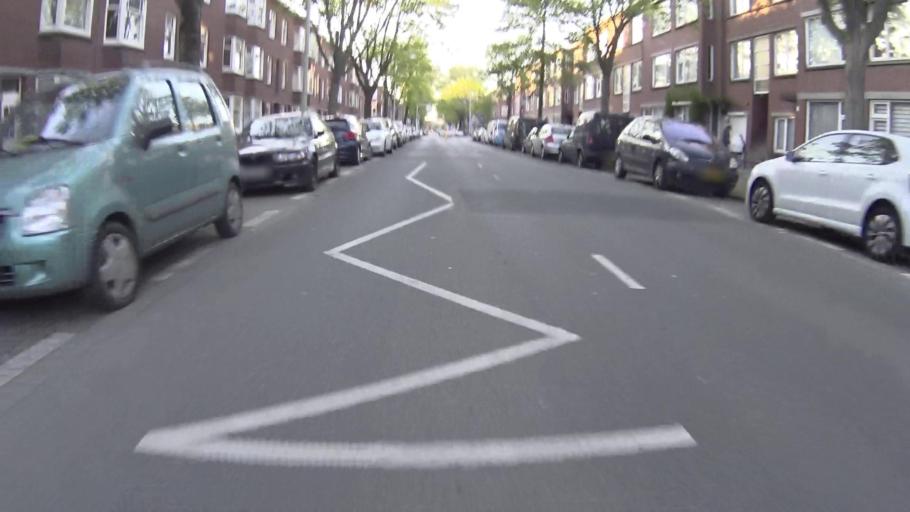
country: NL
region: South Holland
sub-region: Gemeente Rijswijk
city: Rijswijk
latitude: 52.0580
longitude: 4.3297
